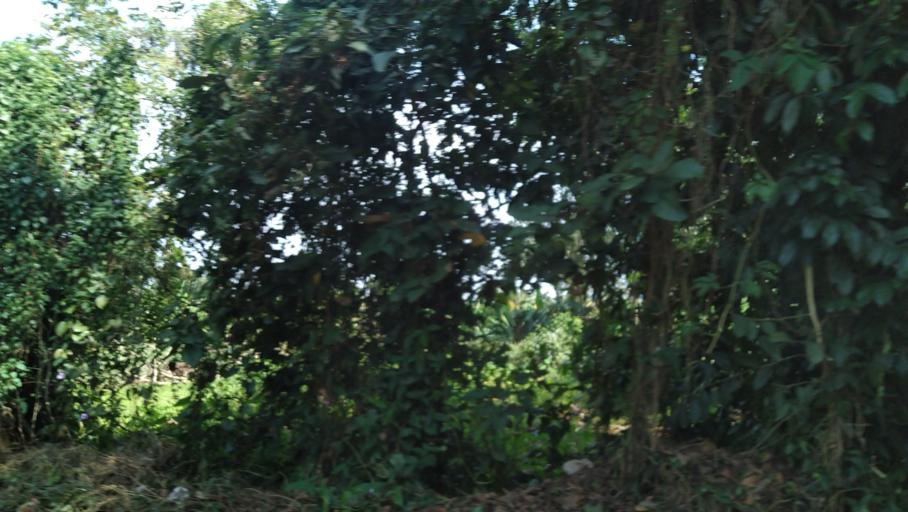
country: IN
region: Kerala
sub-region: Ernakulam
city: Aluva
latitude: 10.1242
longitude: 76.3539
